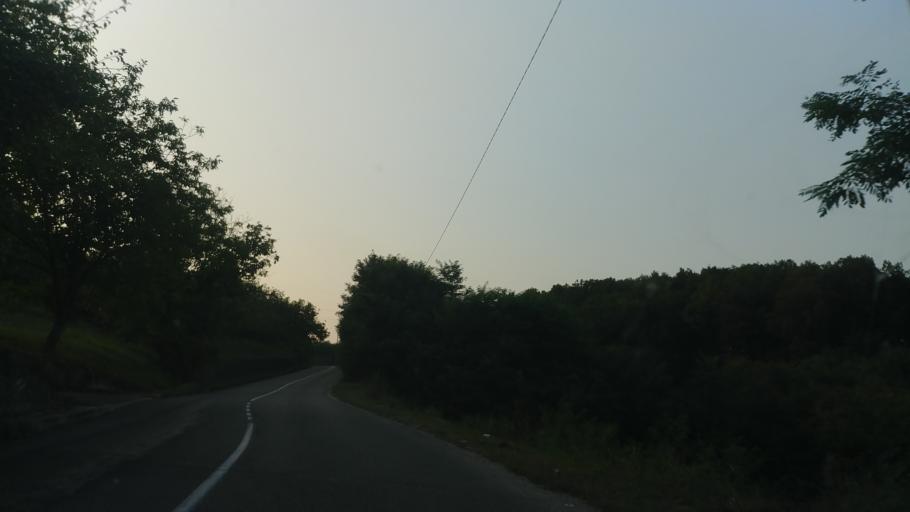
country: BA
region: Republika Srpska
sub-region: Opstina Ugljevik
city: Ugljevik
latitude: 44.7025
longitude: 18.9920
